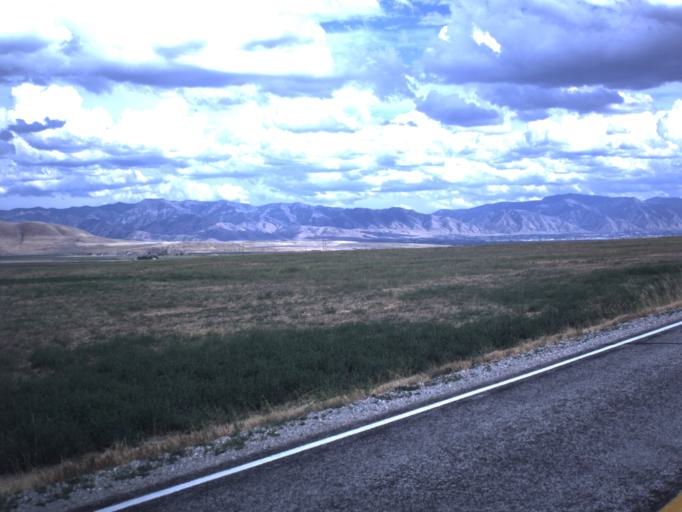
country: US
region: Utah
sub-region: Cache County
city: Benson
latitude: 41.8945
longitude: -112.0426
